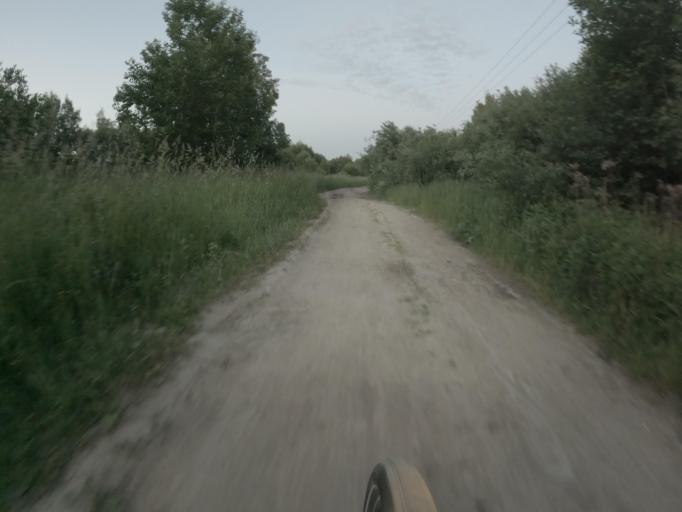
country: RU
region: Leningrad
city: Imeni Sverdlova
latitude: 59.7822
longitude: 30.6851
